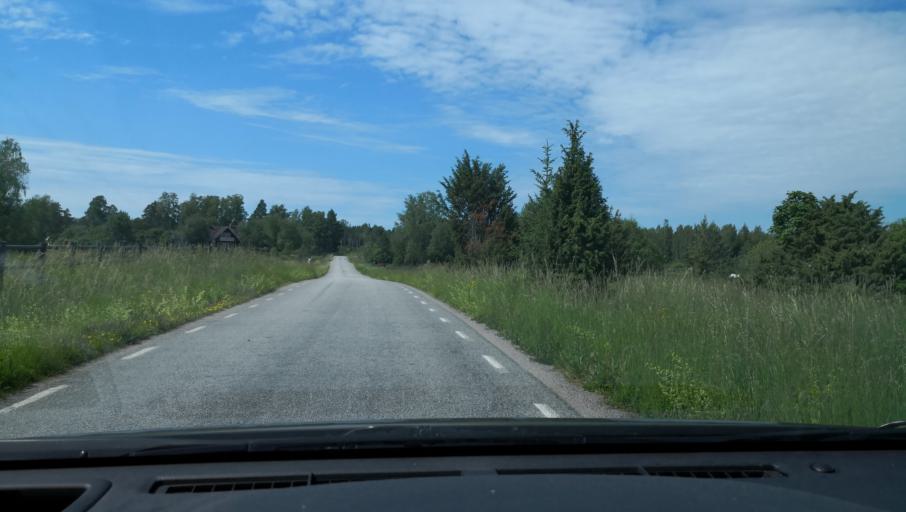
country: SE
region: Stockholm
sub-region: Sigtuna Kommun
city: Sigtuna
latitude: 59.6832
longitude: 17.6793
